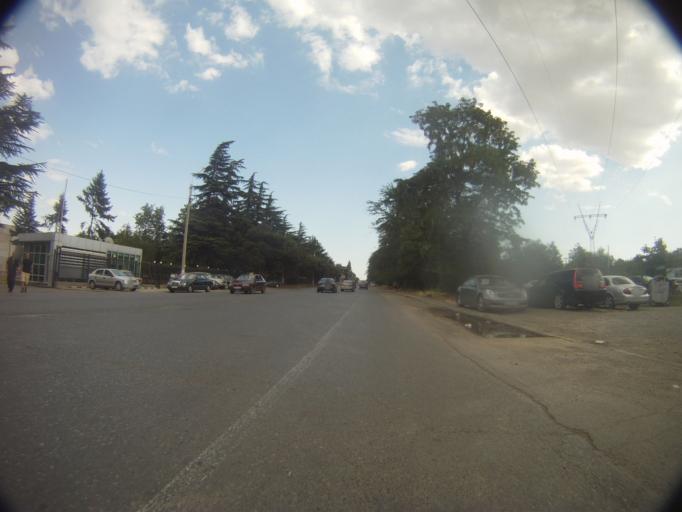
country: GE
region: T'bilisi
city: Tbilisi
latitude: 41.6466
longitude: 44.9103
